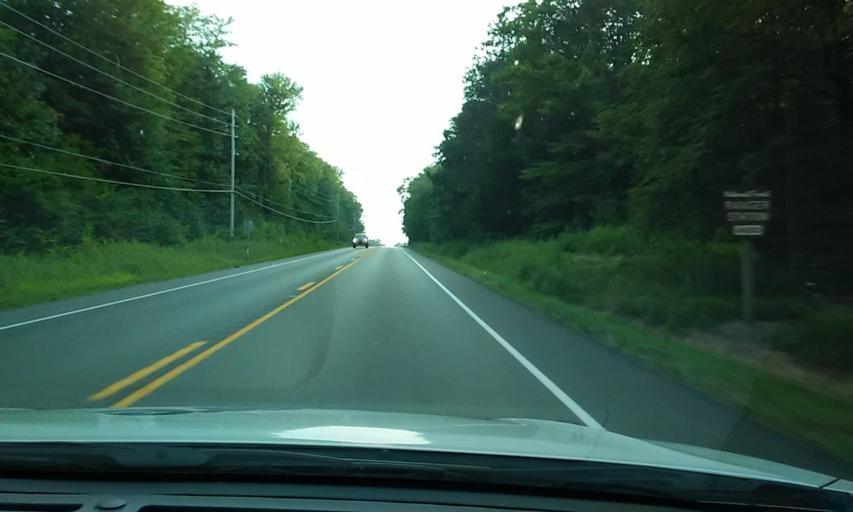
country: US
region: Pennsylvania
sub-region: Forest County
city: Marienville
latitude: 41.4874
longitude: -79.0993
